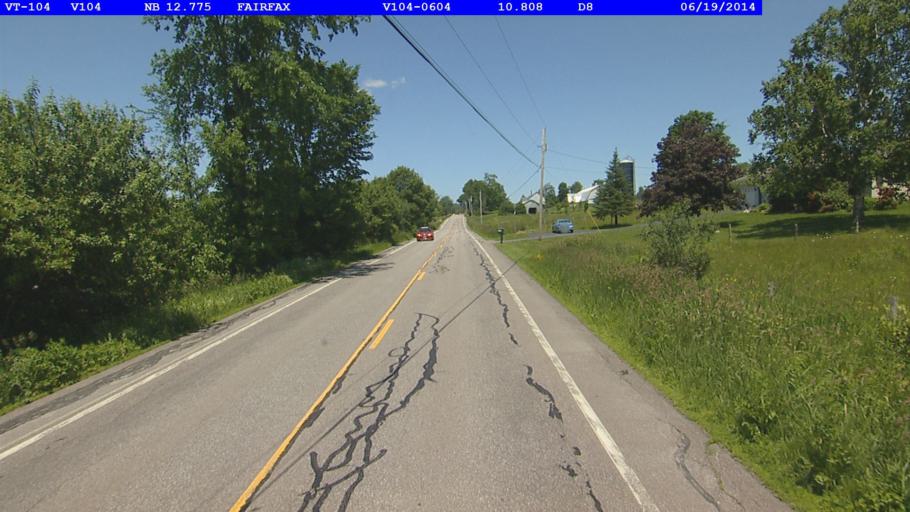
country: US
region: Vermont
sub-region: Franklin County
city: Saint Albans
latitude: 44.7396
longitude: -73.0498
